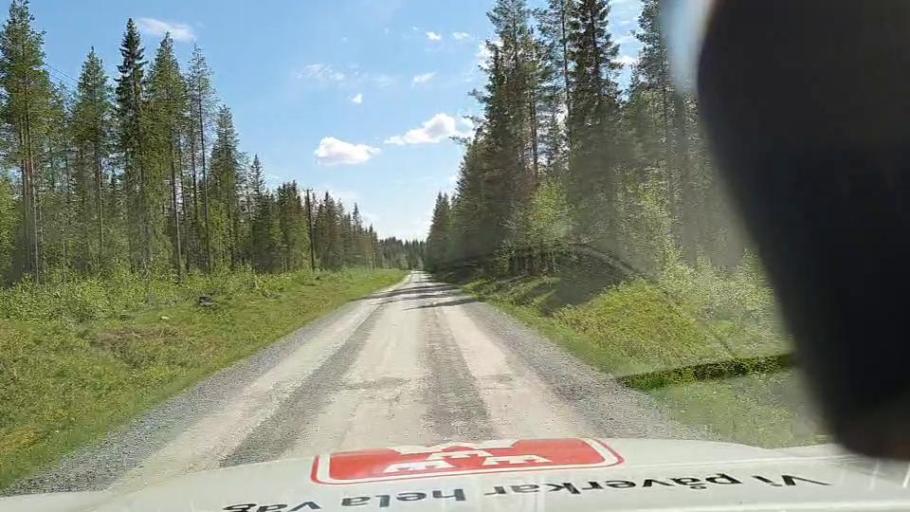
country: SE
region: Jaemtland
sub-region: Stroemsunds Kommun
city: Stroemsund
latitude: 64.4706
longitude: 15.5942
